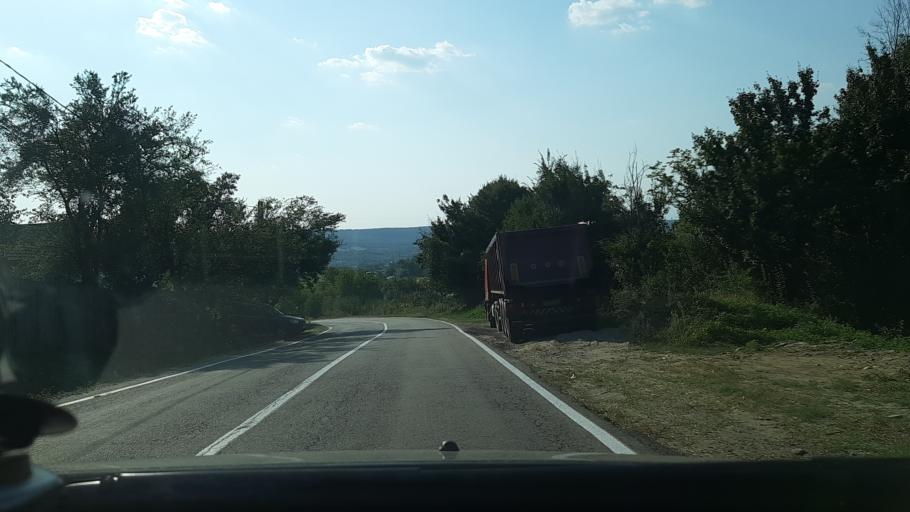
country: RO
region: Gorj
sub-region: Comuna Targu Carbunesti
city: Targu Carbunesti
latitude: 44.9428
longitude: 23.5332
